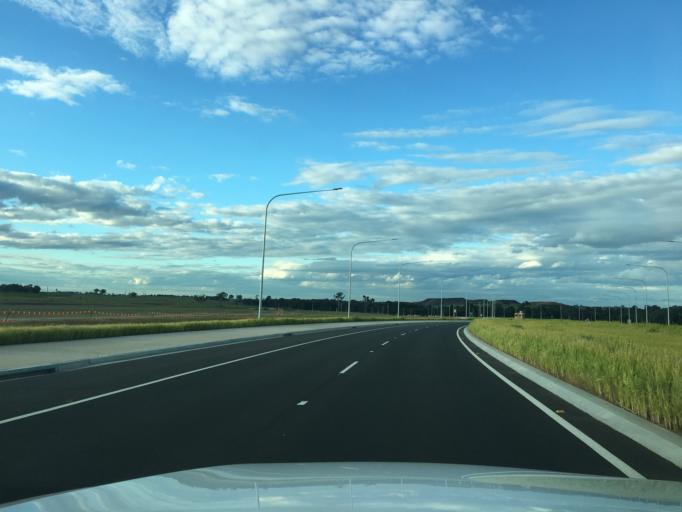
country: AU
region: New South Wales
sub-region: Liverpool
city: Bringelly
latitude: -33.8788
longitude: 150.7464
